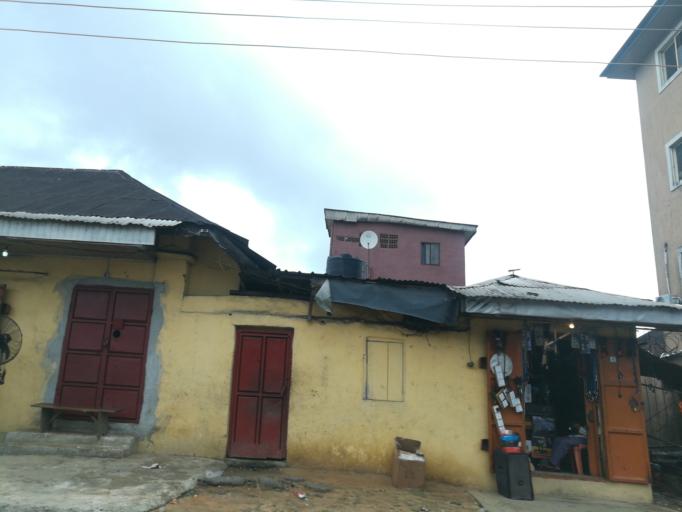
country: NG
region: Rivers
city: Port Harcourt
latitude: 4.7600
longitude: 7.0309
